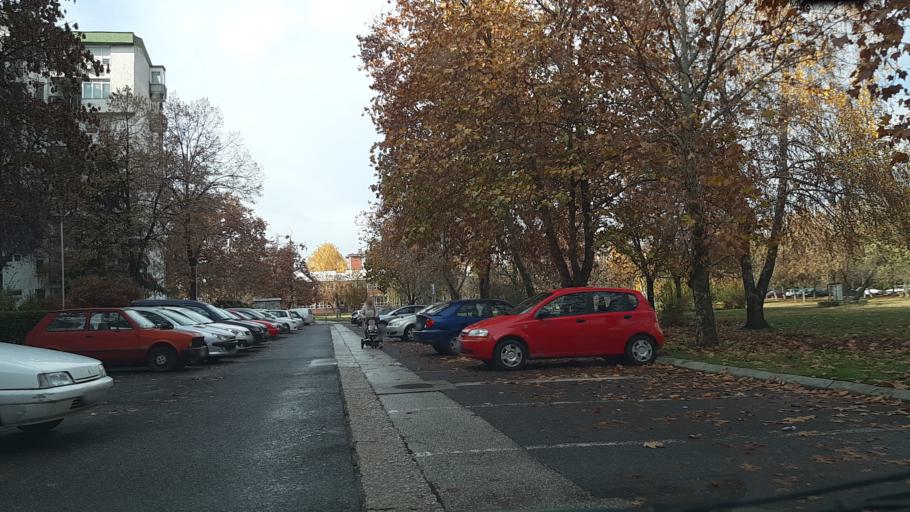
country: MK
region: Kisela Voda
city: Usje
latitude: 41.9883
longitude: 21.4670
